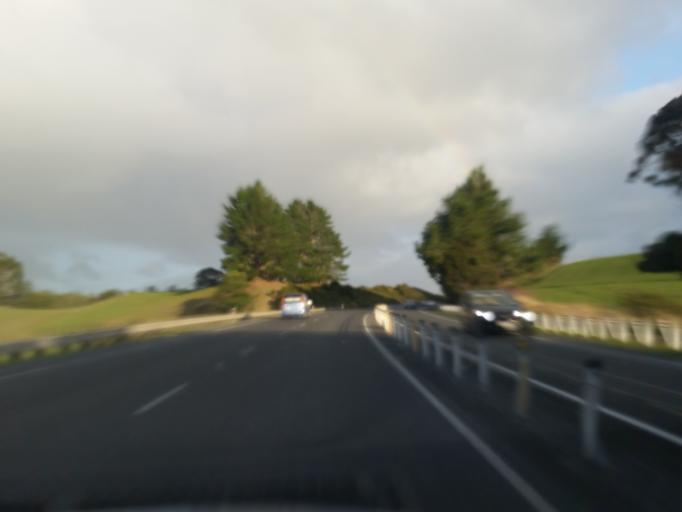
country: NZ
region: Waikato
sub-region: Waikato District
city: Te Kauwhata
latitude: -37.3657
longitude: 175.0919
